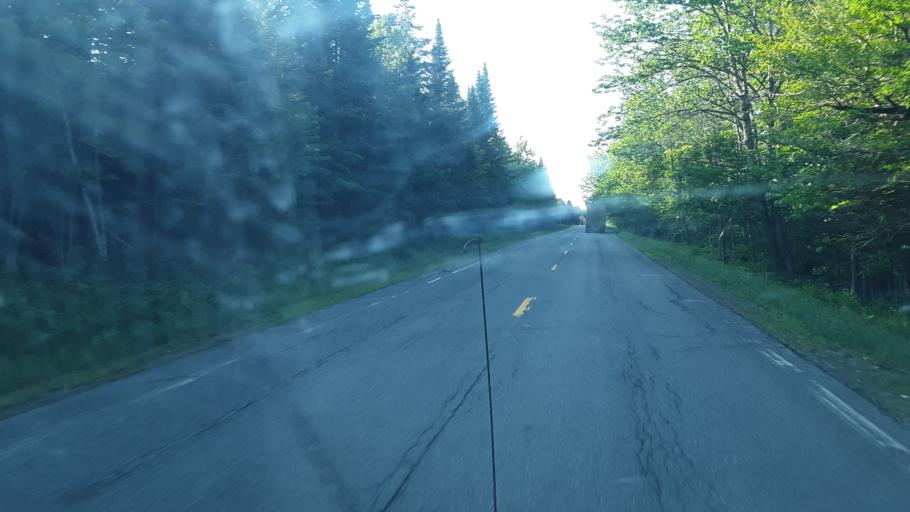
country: US
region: Maine
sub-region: Penobscot County
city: Patten
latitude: 46.1884
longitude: -68.2557
